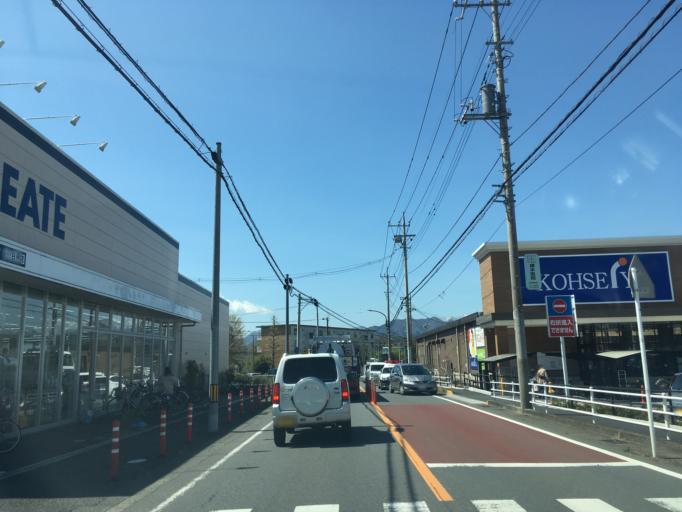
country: JP
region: Tokyo
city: Hachioji
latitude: 35.5815
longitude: 139.3372
